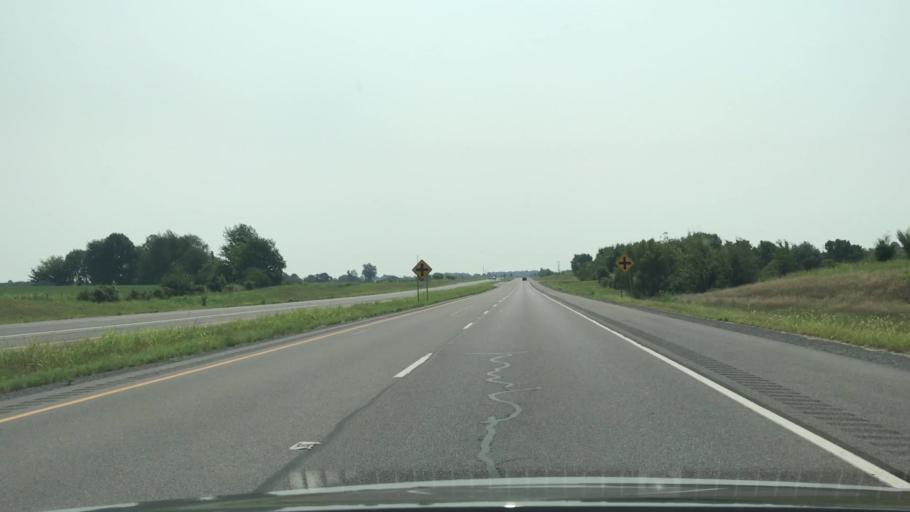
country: US
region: Kentucky
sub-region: Graves County
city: Mayfield
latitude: 36.6878
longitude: -88.5463
